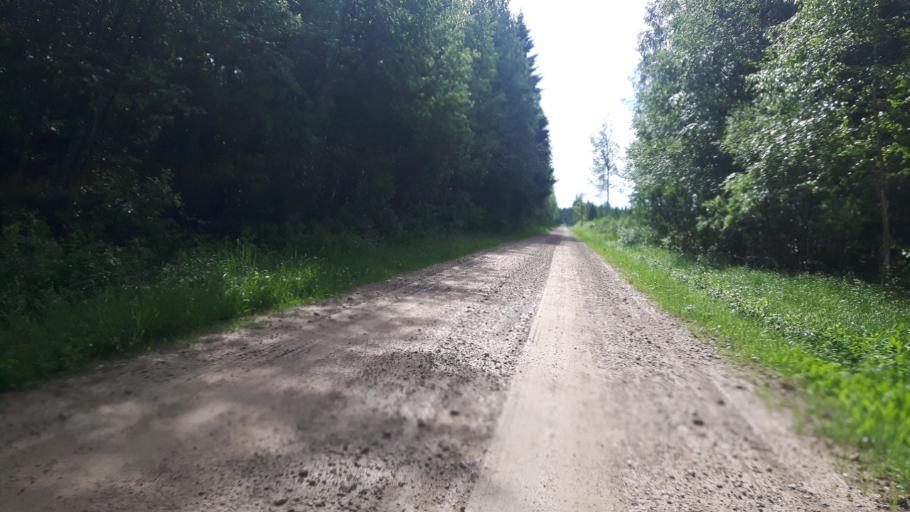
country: EE
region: Paernumaa
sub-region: Vaendra vald (alev)
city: Vandra
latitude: 58.7361
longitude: 24.9979
